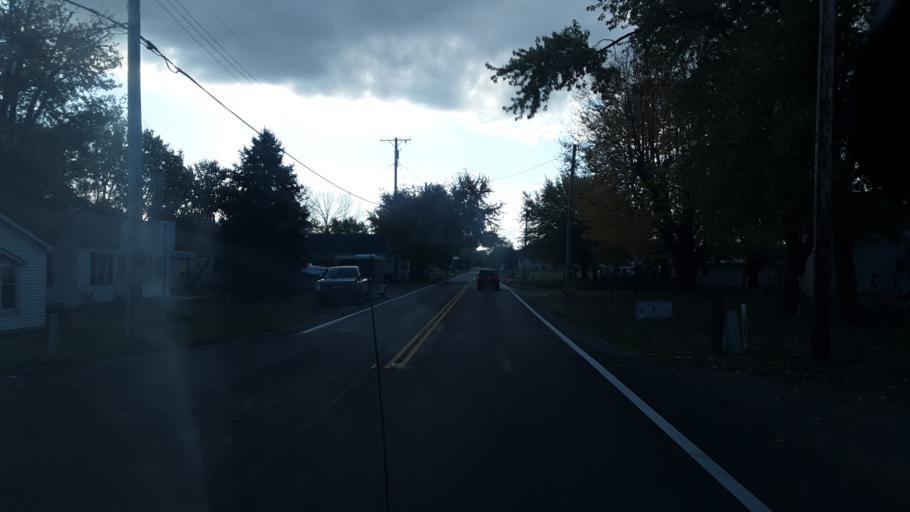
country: US
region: Ohio
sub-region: Fayette County
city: Washington Court House
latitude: 39.5487
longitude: -83.4495
